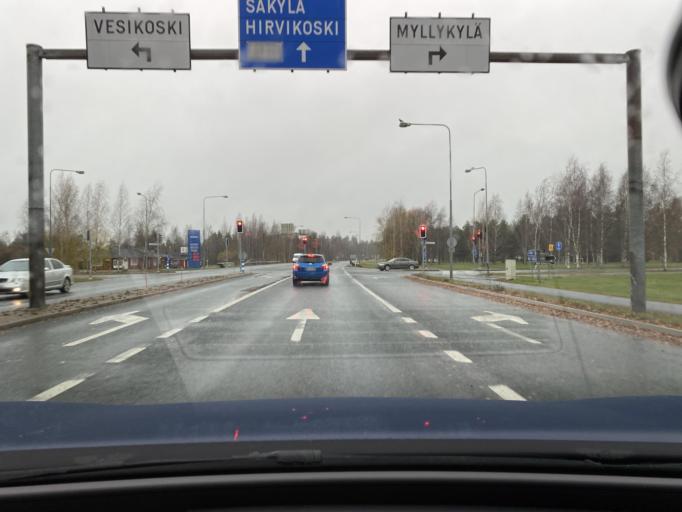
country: FI
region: Varsinais-Suomi
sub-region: Loimaa
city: Loimaa
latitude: 60.8599
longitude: 23.0285
